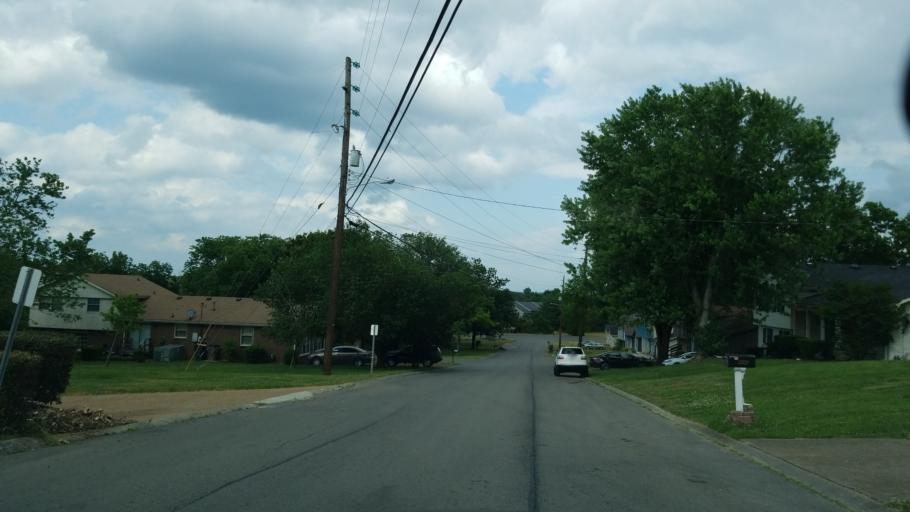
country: US
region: Tennessee
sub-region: Rutherford County
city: La Vergne
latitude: 36.0836
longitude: -86.6078
